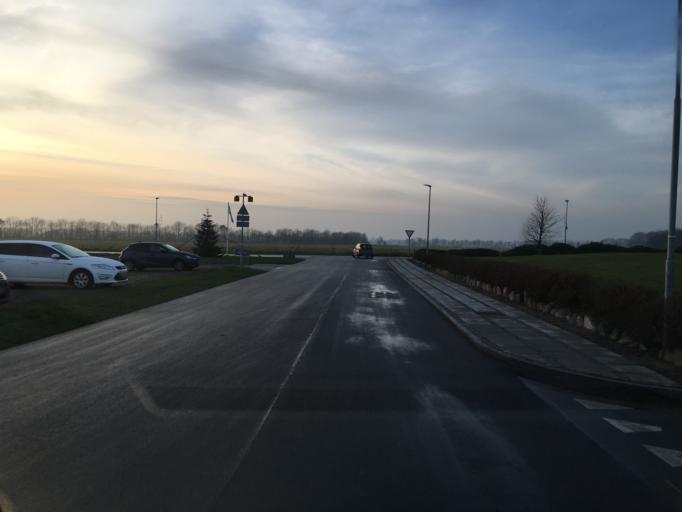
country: DK
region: South Denmark
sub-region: Tonder Kommune
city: Toftlund
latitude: 55.1262
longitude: 9.0635
